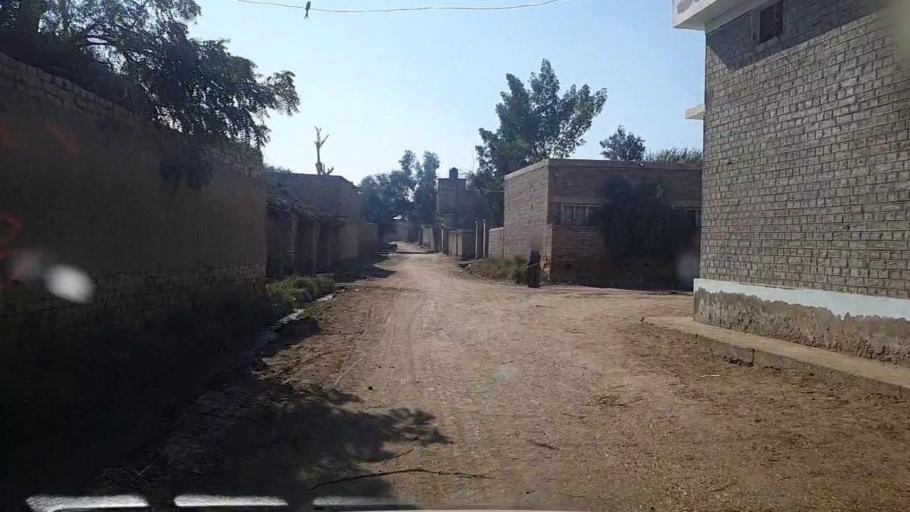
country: PK
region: Sindh
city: Khairpur
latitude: 27.9576
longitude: 69.6863
